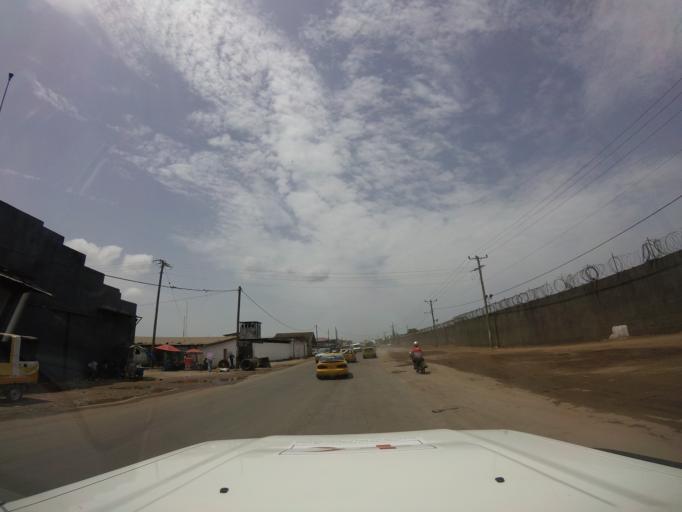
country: LR
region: Montserrado
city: Monrovia
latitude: 6.3420
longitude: -10.7912
